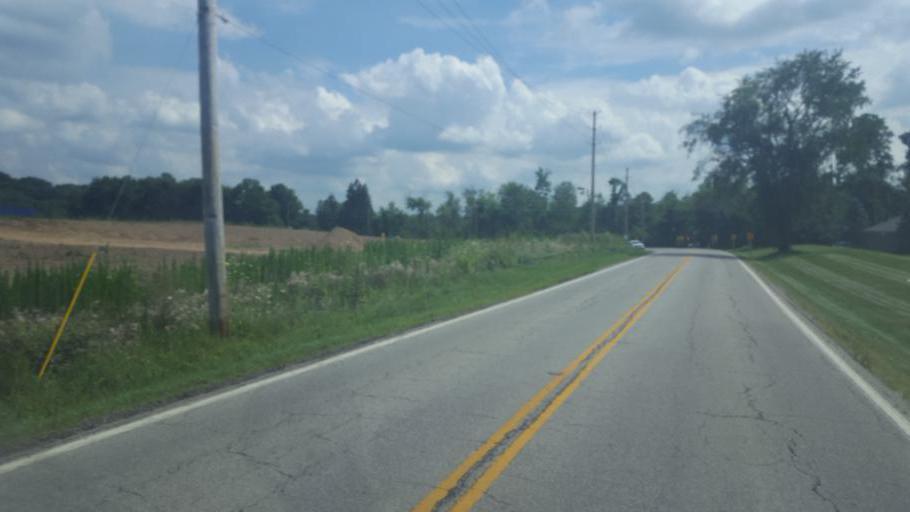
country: US
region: Ohio
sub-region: Richland County
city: Lexington
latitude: 40.6761
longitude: -82.5697
